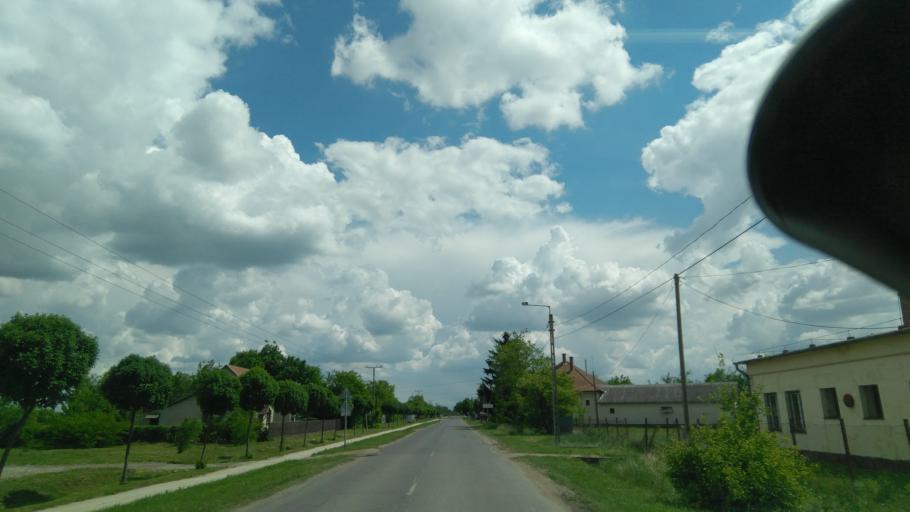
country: HU
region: Bekes
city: Devavanya
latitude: 47.0414
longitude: 20.9415
